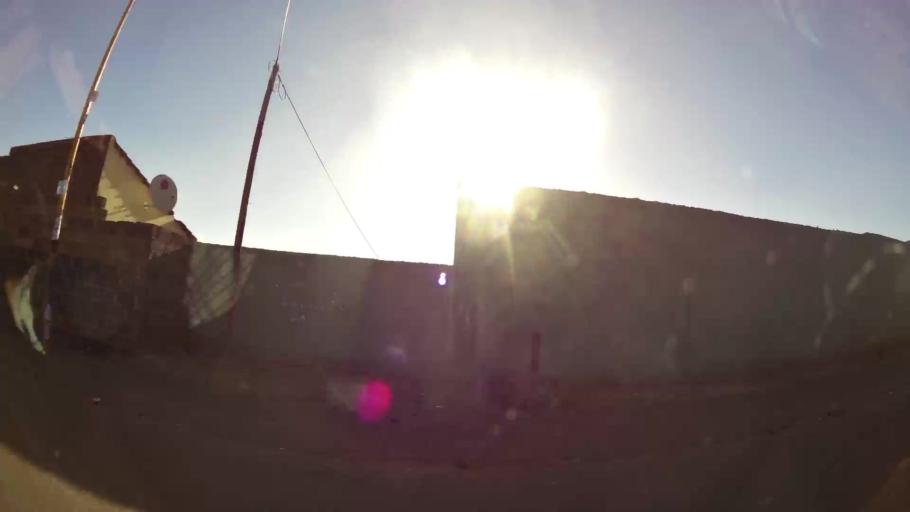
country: ZA
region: Gauteng
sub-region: Ekurhuleni Metropolitan Municipality
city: Tembisa
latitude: -26.0254
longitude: 28.2145
